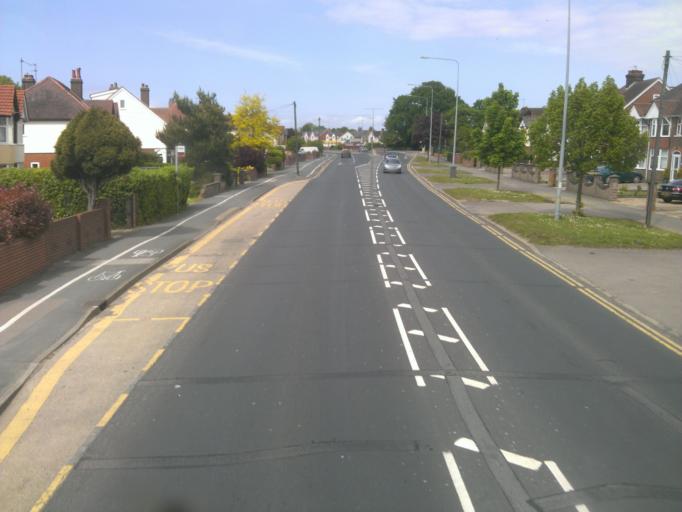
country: GB
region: England
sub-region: Essex
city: Colchester
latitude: 51.9007
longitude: 0.9220
